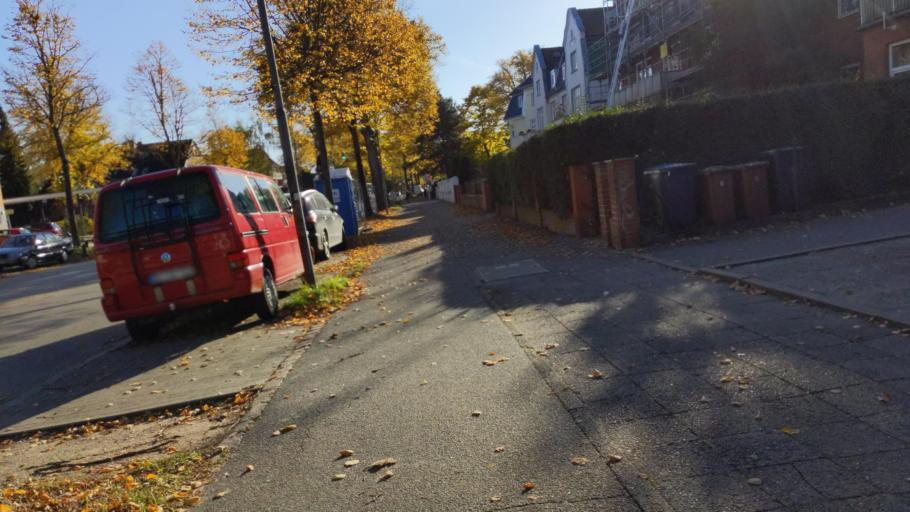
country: DE
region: Schleswig-Holstein
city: Luebeck
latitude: 53.8676
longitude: 10.7121
